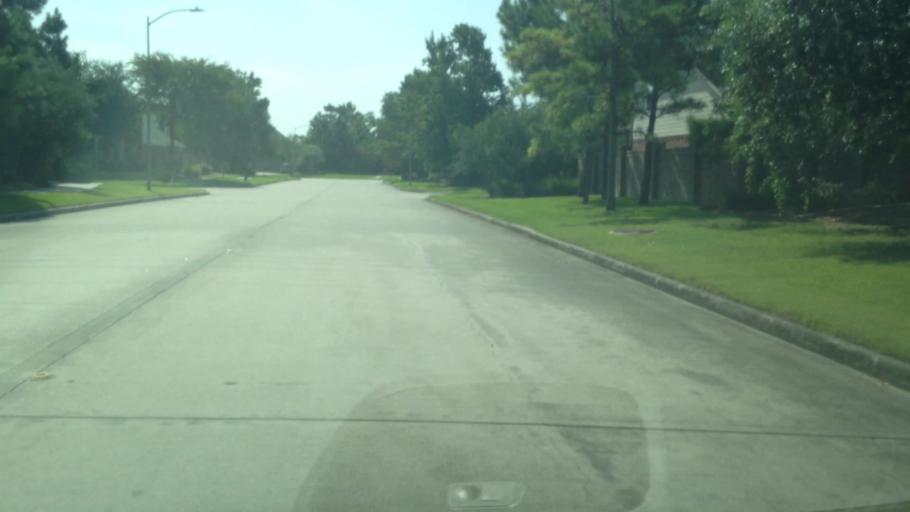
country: US
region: Texas
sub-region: Harris County
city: Sheldon
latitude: 29.9232
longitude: -95.1722
